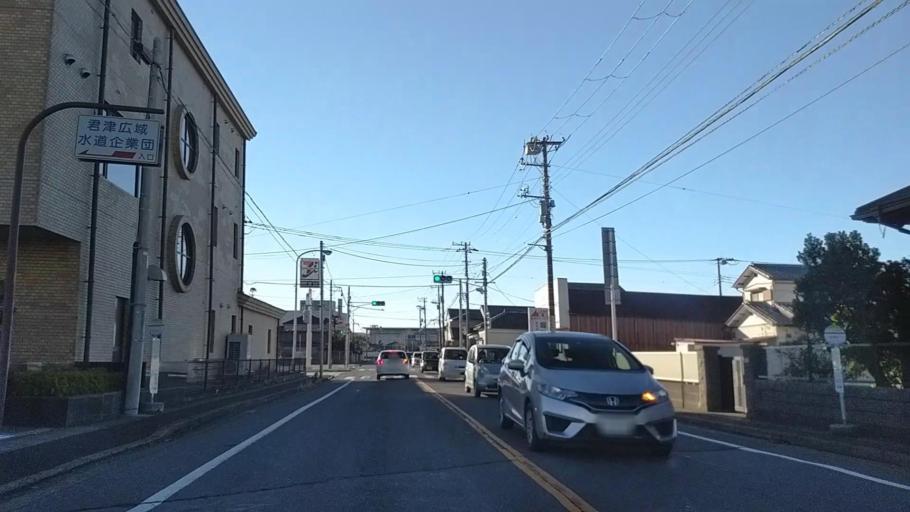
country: JP
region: Chiba
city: Kisarazu
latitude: 35.3781
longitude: 139.9186
